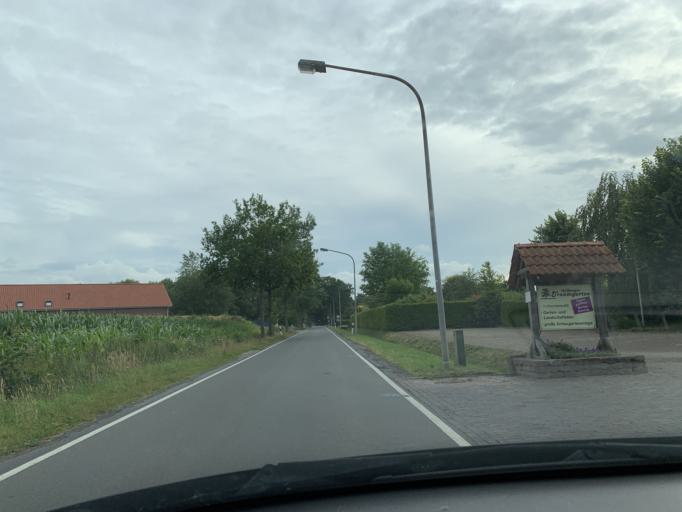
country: DE
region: Lower Saxony
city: Westerstede
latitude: 53.2762
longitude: 7.9063
